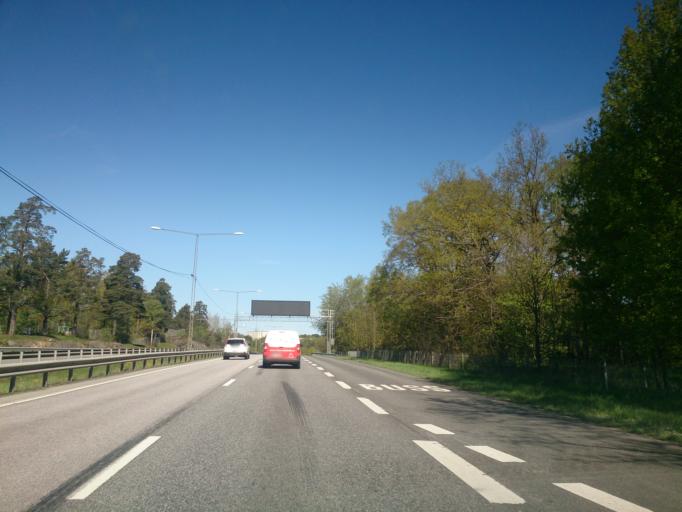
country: SE
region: Stockholm
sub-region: Stockholms Kommun
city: Arsta
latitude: 59.2462
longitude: 18.1030
